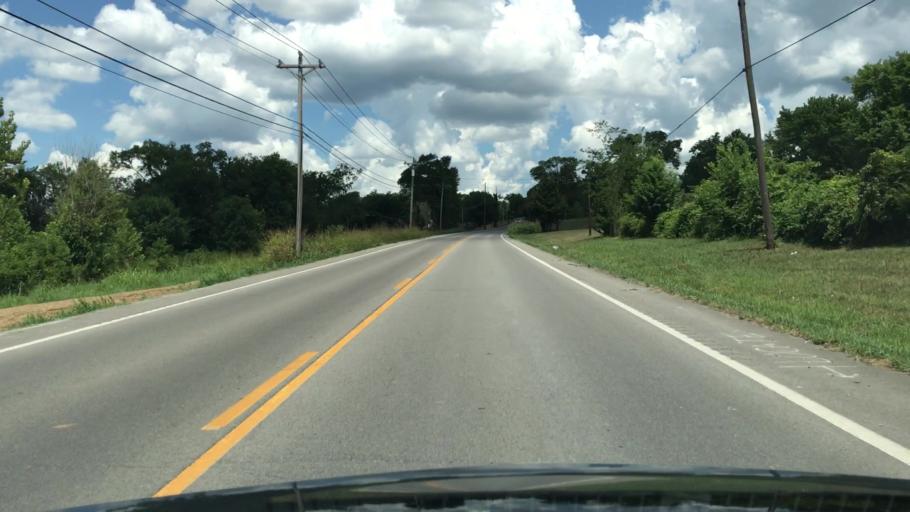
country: US
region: Tennessee
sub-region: Williamson County
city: Nolensville
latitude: 35.8934
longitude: -86.6658
